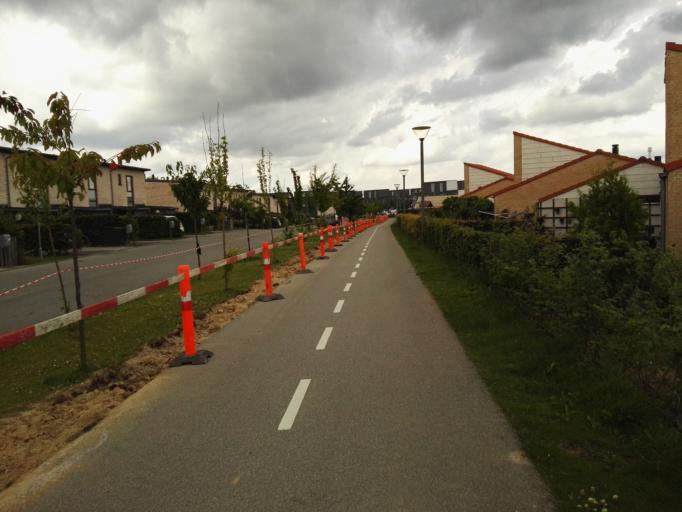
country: DK
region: Capital Region
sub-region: Egedal Kommune
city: Stenlose
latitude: 55.7620
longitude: 12.1758
